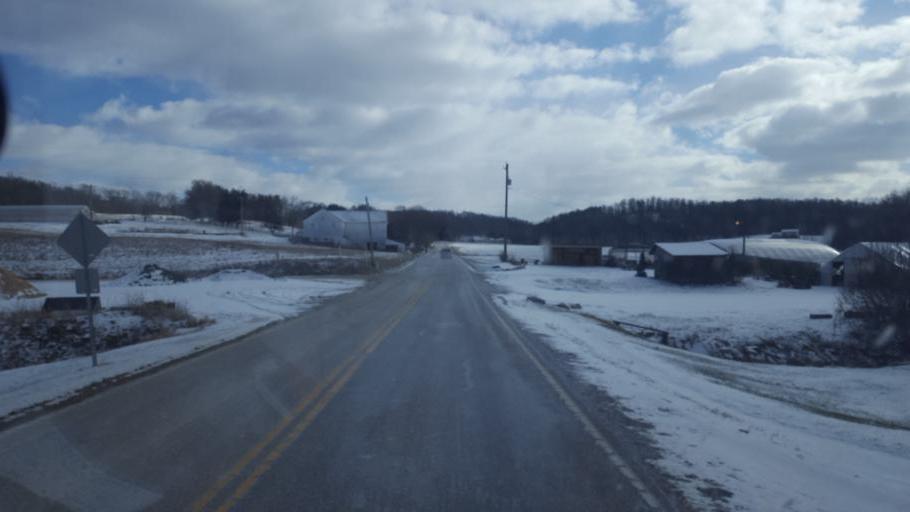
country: US
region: Ohio
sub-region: Coshocton County
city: West Lafayette
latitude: 40.3198
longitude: -81.8062
